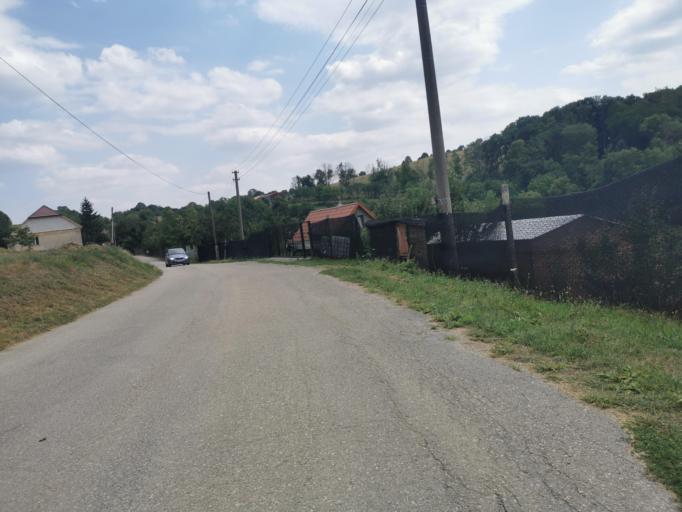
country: SK
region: Nitriansky
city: Brezova pod Bradlom
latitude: 48.6634
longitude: 17.4777
